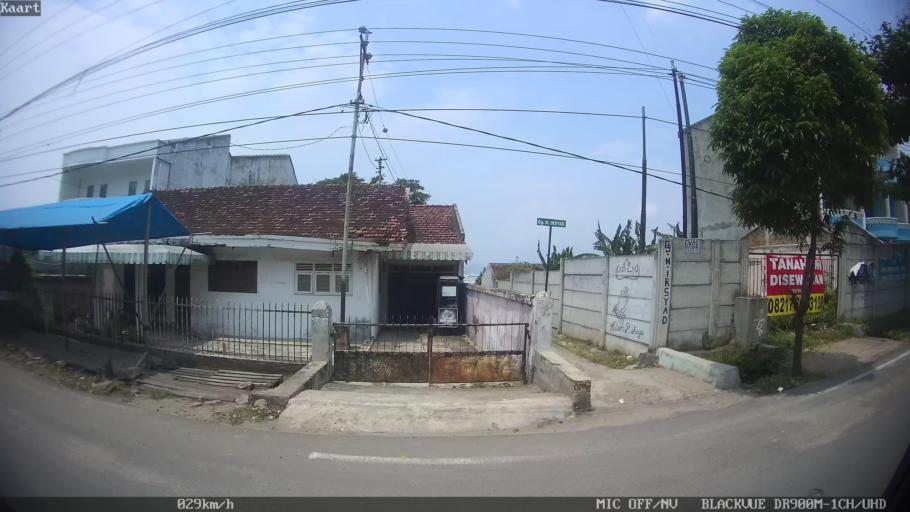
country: ID
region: Lampung
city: Bandarlampung
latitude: -5.4360
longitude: 105.2821
